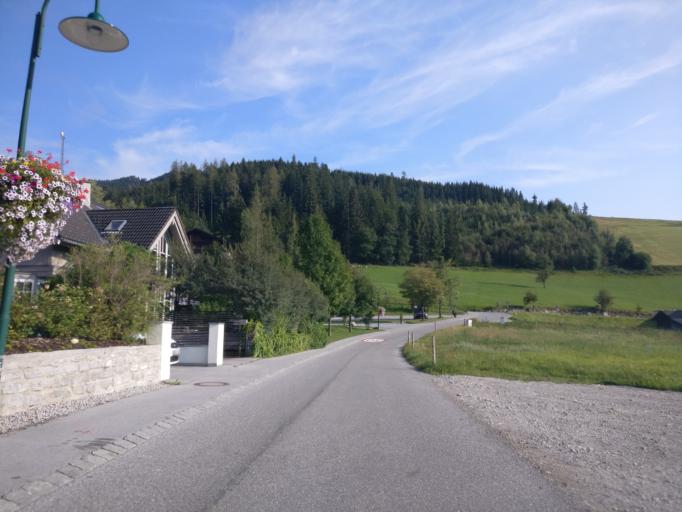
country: AT
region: Salzburg
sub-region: Politischer Bezirk Sankt Johann im Pongau
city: Werfenweng
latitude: 47.4614
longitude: 13.2537
